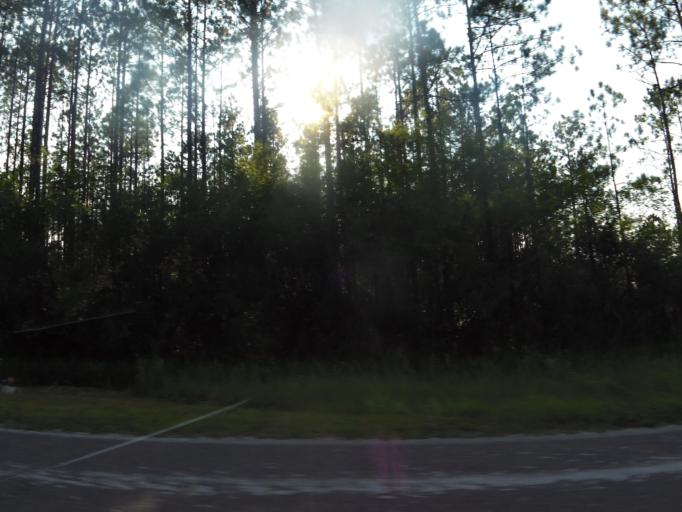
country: US
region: Florida
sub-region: Duval County
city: Baldwin
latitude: 30.3492
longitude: -82.0093
